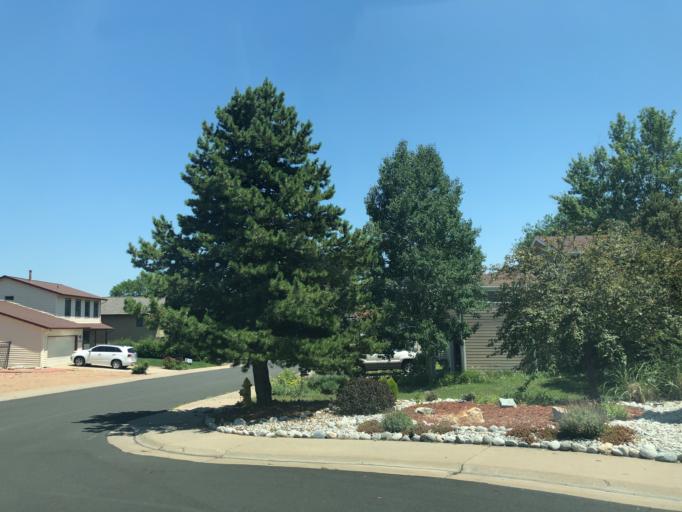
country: US
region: Colorado
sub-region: Arapahoe County
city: Dove Valley
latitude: 39.6238
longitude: -104.7844
